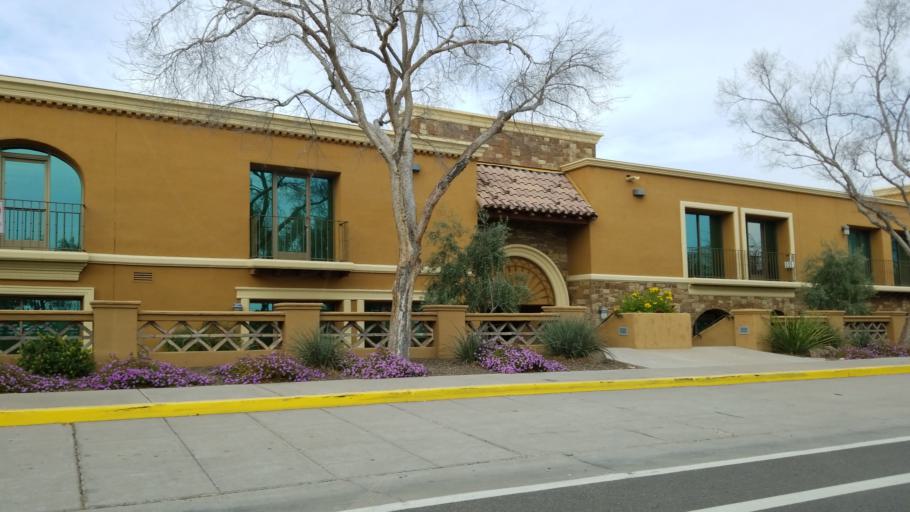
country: US
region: Arizona
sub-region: Maricopa County
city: Paradise Valley
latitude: 33.5867
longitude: -111.9272
